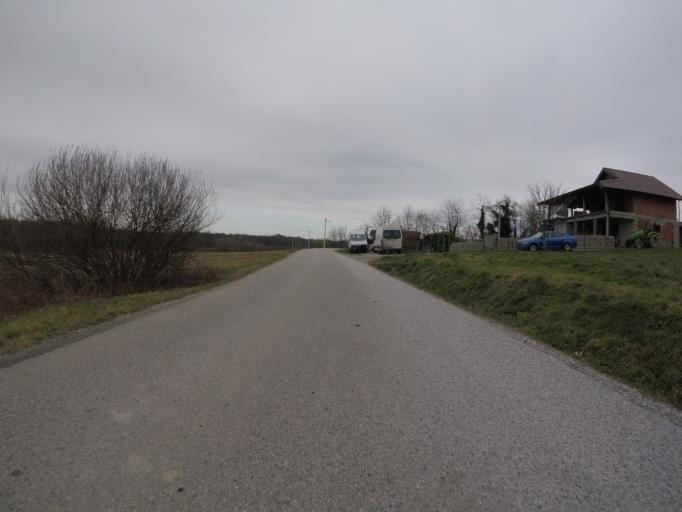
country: HR
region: Grad Zagreb
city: Strmec
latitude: 45.6694
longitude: 15.8942
